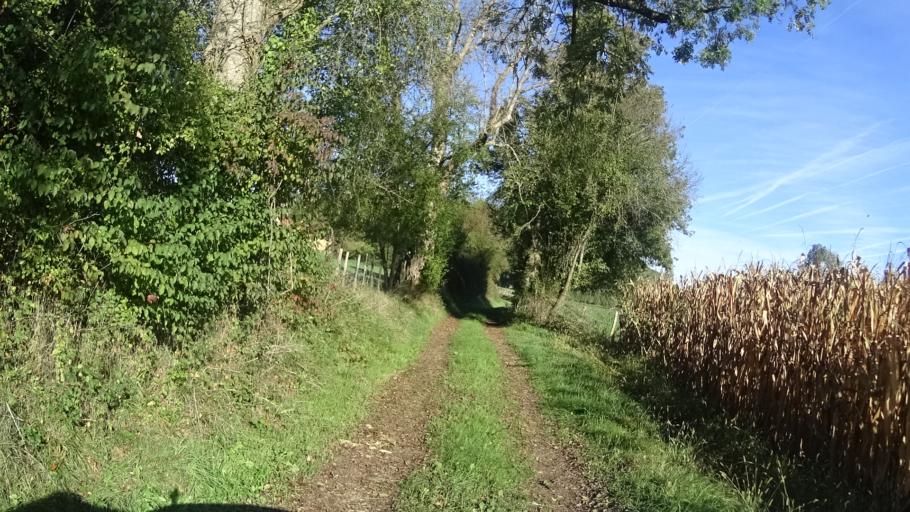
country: FR
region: Aquitaine
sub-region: Departement de la Dordogne
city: Saint-Cyprien
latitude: 44.8409
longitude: 1.0170
